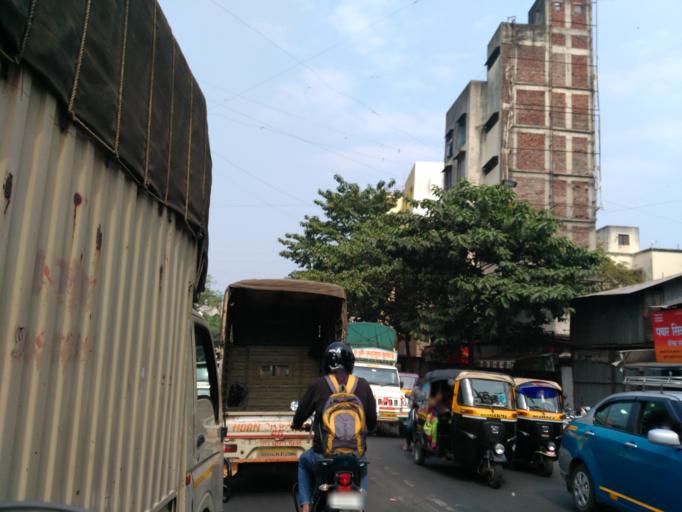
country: IN
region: Maharashtra
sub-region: Pune Division
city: Pune
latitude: 18.5168
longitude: 73.8685
